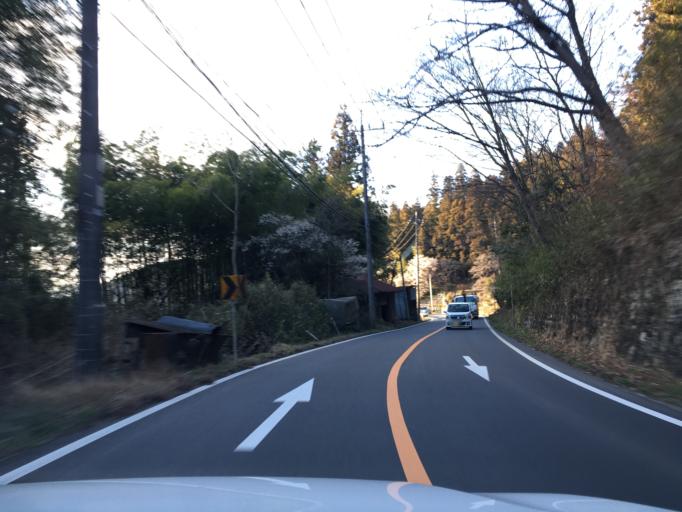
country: JP
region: Tochigi
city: Otawara
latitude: 36.8621
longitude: 140.1698
